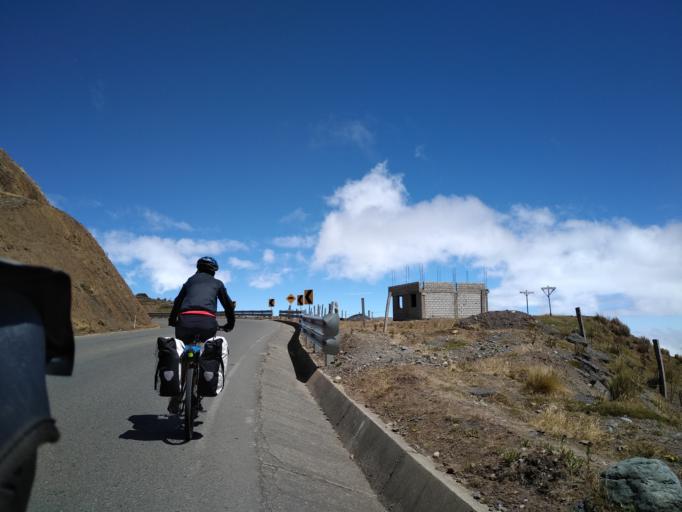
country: EC
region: Cotopaxi
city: Pujili
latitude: -0.9685
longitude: -78.9285
